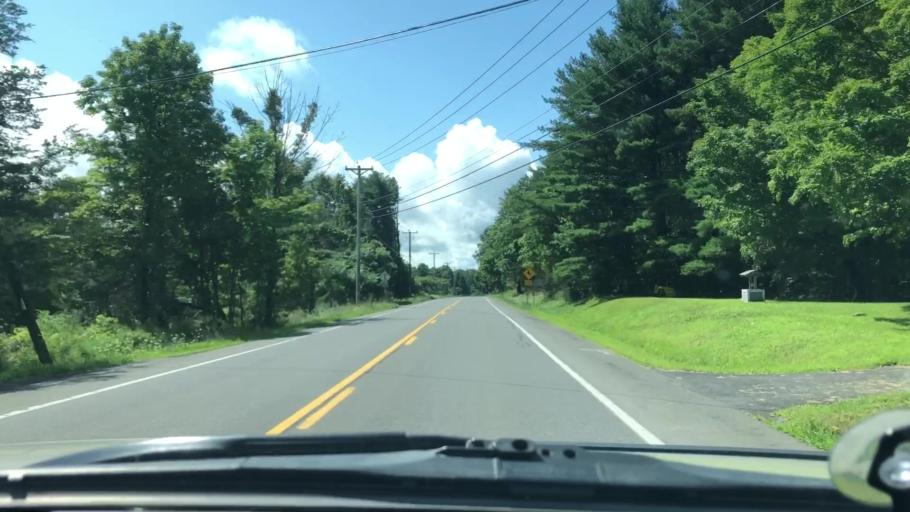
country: US
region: New York
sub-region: Greene County
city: Cairo
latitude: 42.2334
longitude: -73.9829
